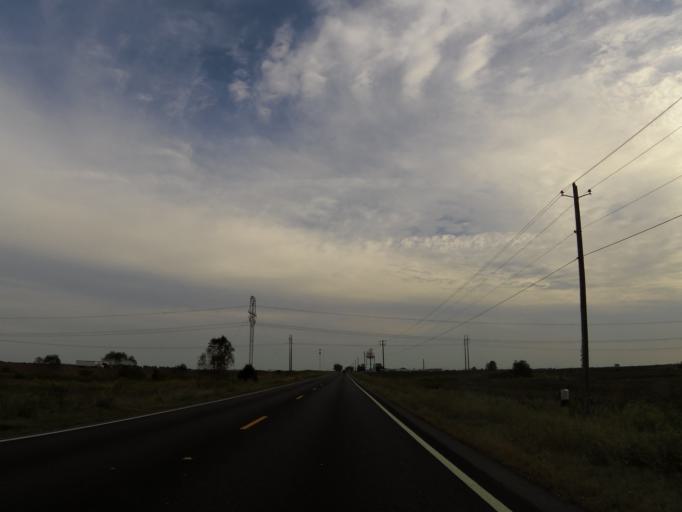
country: US
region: Alabama
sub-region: Escambia County
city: Atmore
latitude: 31.1681
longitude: -87.4637
